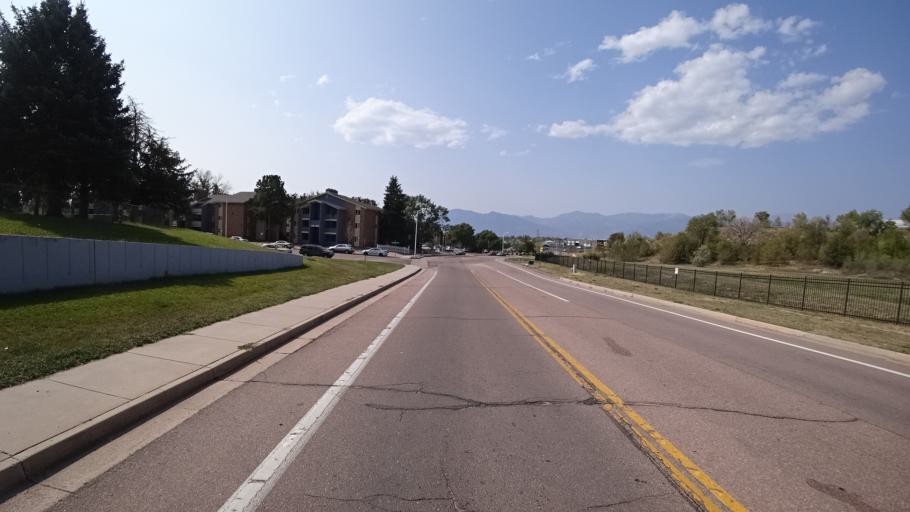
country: US
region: Colorado
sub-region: El Paso County
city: Cimarron Hills
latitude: 38.8362
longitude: -104.7525
